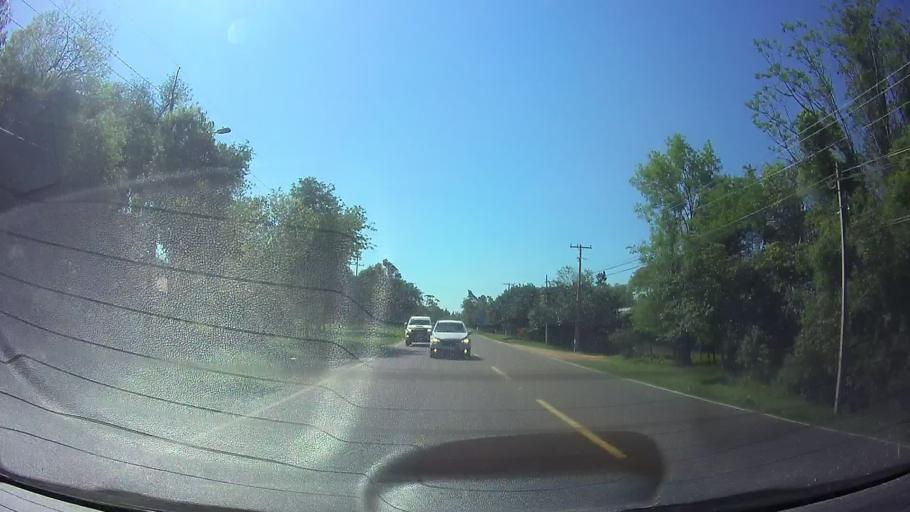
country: PY
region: Cordillera
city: San Bernardino
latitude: -25.3460
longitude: -57.2723
